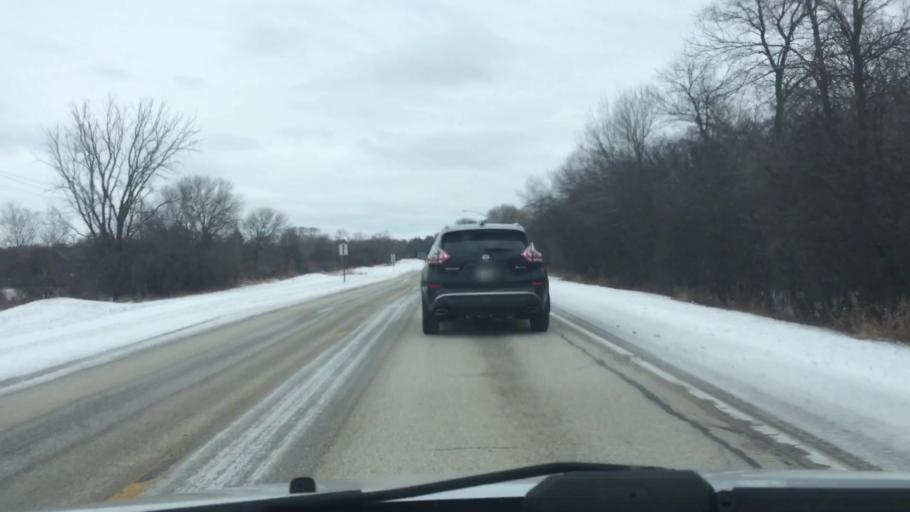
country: US
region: Wisconsin
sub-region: Waukesha County
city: Brookfield
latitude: 43.0479
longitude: -88.1060
